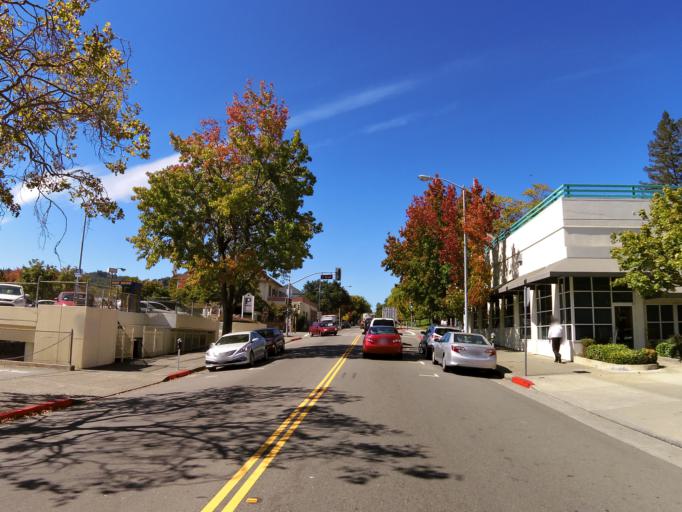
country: US
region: California
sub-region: Marin County
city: San Rafael
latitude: 37.9744
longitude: -122.5299
